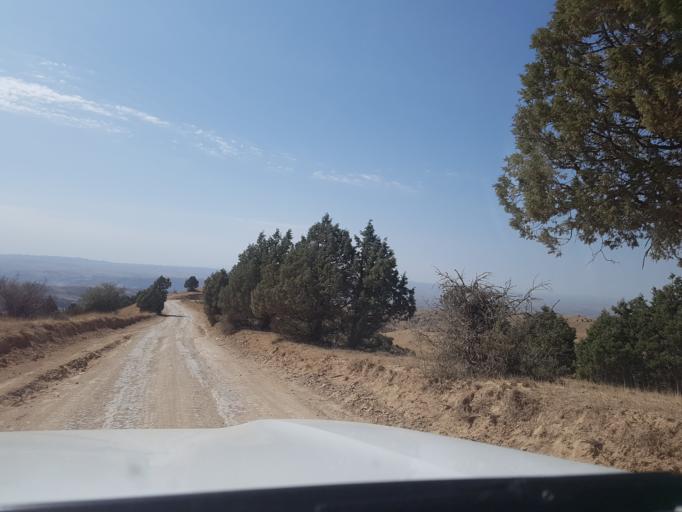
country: TM
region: Ahal
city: Baharly
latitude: 38.3076
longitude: 56.9487
